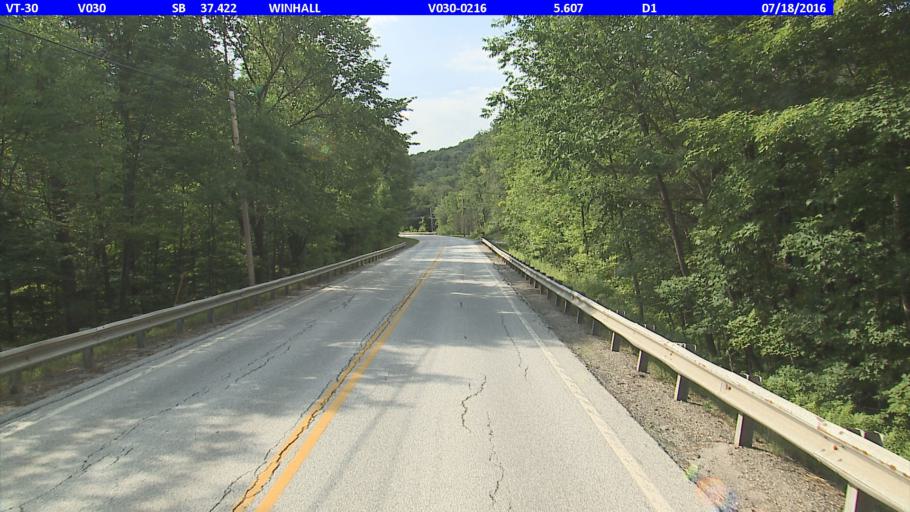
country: US
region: Vermont
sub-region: Bennington County
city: Manchester Center
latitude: 43.1873
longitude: -72.9365
